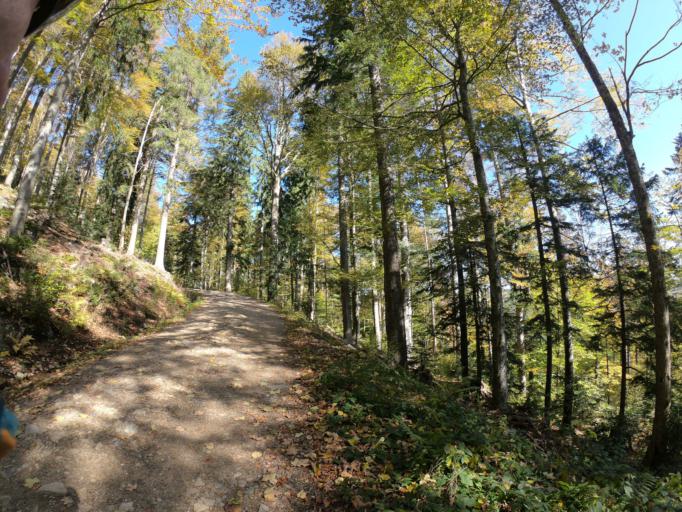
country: DE
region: Bavaria
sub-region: Lower Bavaria
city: Bayerisch Eisenstein
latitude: 49.1041
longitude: 13.1524
